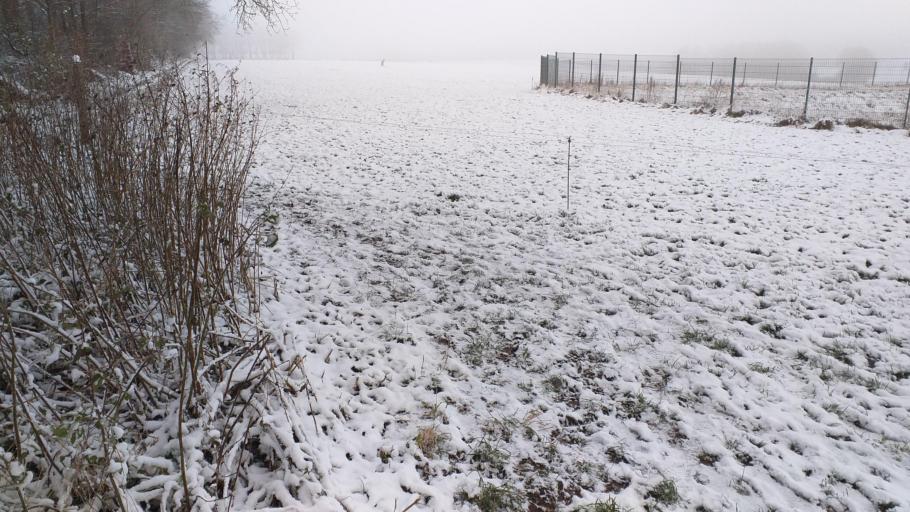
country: DE
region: North Rhine-Westphalia
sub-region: Regierungsbezirk Koln
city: Monschau
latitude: 50.5727
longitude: 6.2552
